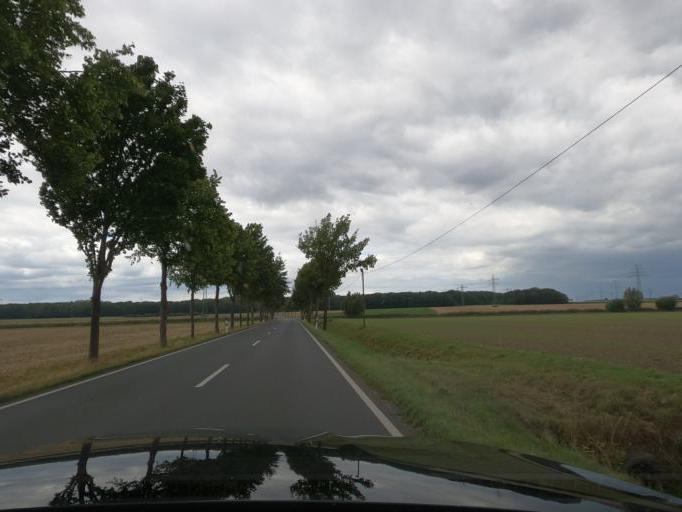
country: DE
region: Lower Saxony
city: Sehnde
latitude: 52.2993
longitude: 9.9029
